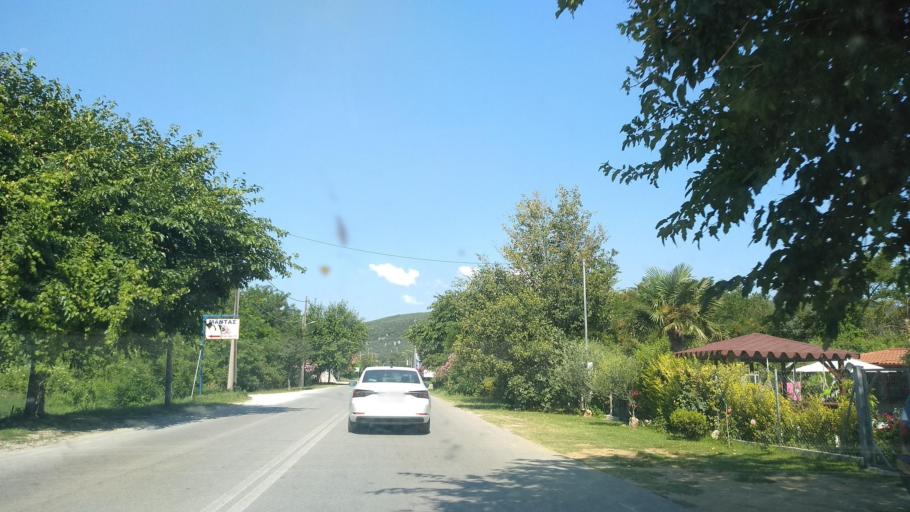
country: GR
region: Central Macedonia
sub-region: Nomos Thessalonikis
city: Stavros
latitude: 40.6683
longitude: 23.6787
